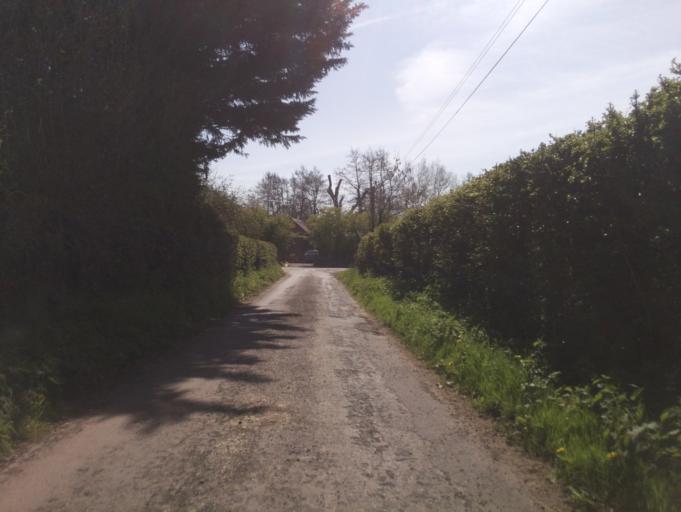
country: GB
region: Wales
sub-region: Monmouthshire
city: Llangwm
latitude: 51.7356
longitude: -2.8170
